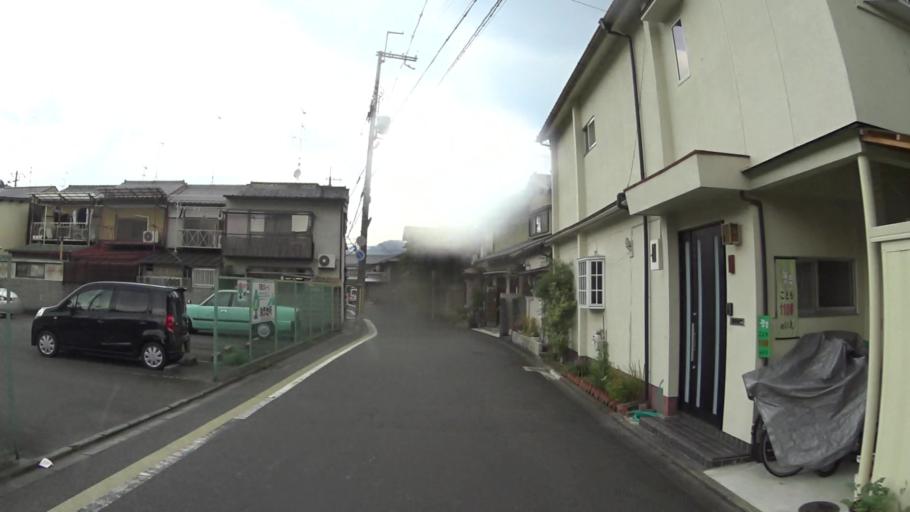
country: JP
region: Kyoto
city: Kyoto
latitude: 35.0206
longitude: 135.7157
